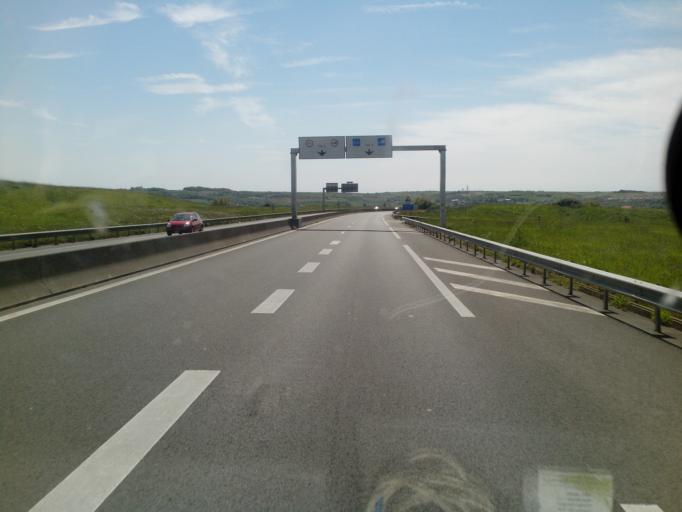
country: FR
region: Nord-Pas-de-Calais
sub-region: Departement du Pas-de-Calais
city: Saint-Leonard
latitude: 50.7057
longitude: 1.6317
